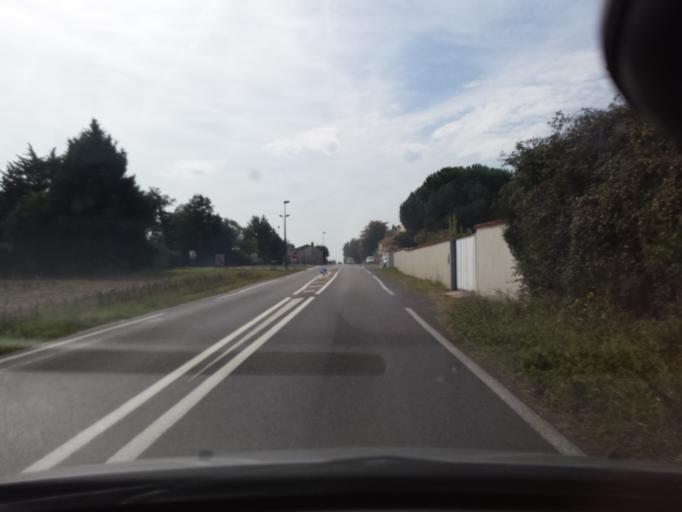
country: FR
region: Pays de la Loire
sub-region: Departement de la Vendee
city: Nieul-le-Dolent
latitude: 46.5256
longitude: -1.5513
